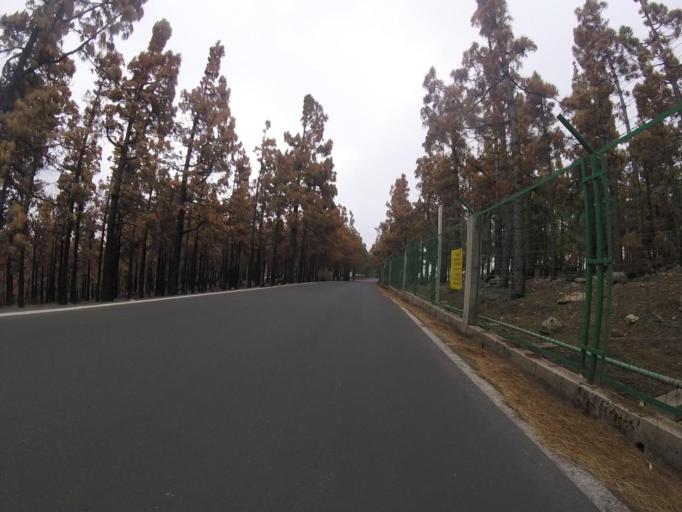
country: ES
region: Canary Islands
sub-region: Provincia de Las Palmas
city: San Bartolome
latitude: 27.9639
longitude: -15.5702
